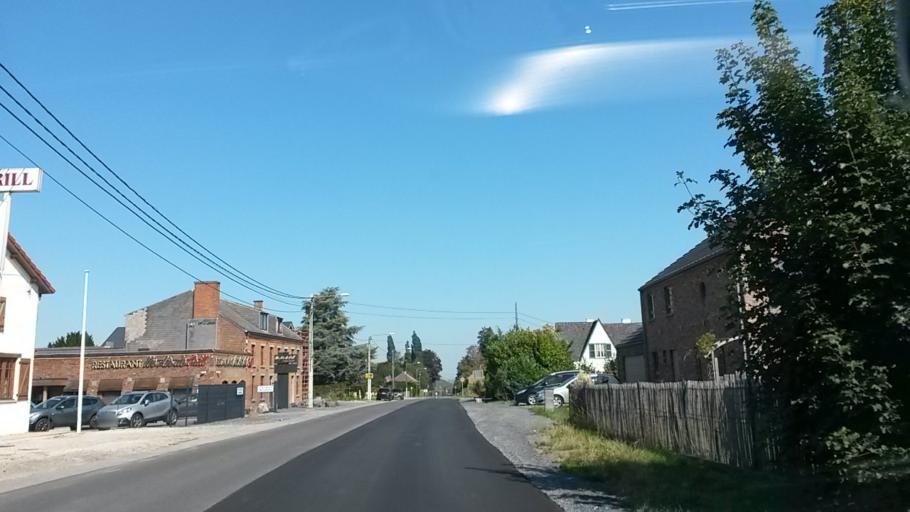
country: BE
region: Wallonia
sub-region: Province du Hainaut
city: Binche
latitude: 50.3905
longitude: 4.1730
